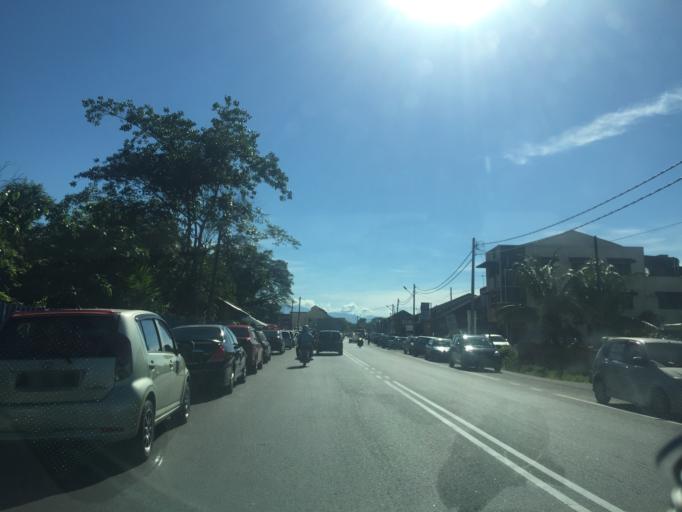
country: MY
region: Penang
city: Tasek Glugor
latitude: 5.5139
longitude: 100.5518
